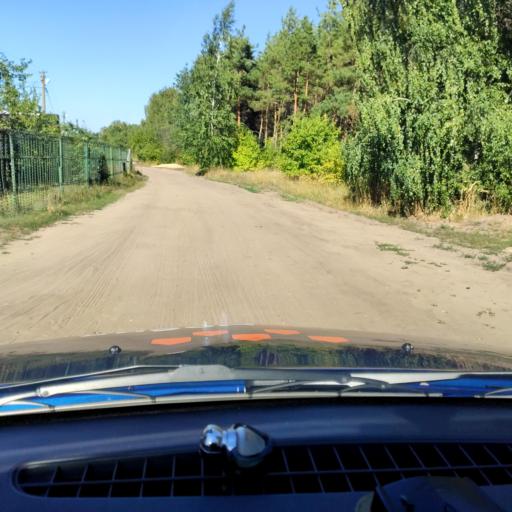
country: RU
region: Voronezj
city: Maslovka
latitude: 51.5440
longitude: 39.1763
